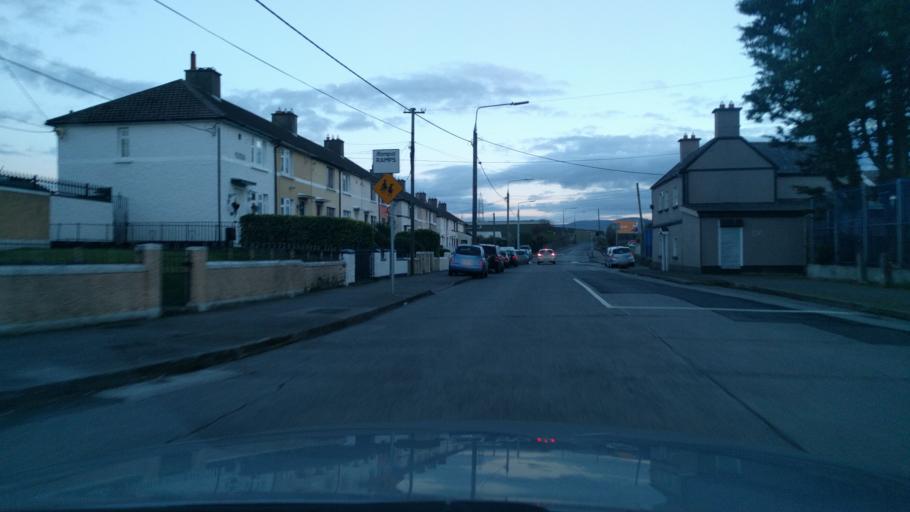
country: IE
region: Leinster
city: Ballyfermot
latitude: 53.3378
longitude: -6.3539
